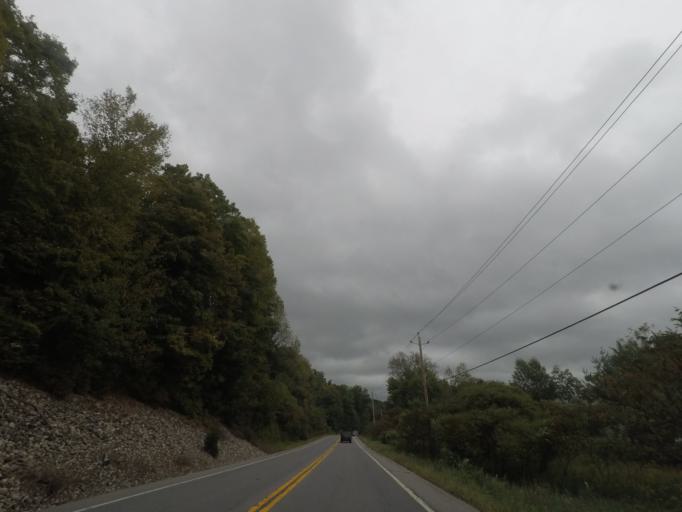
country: US
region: New York
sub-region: Saratoga County
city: Mechanicville
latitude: 42.9230
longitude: -73.7434
